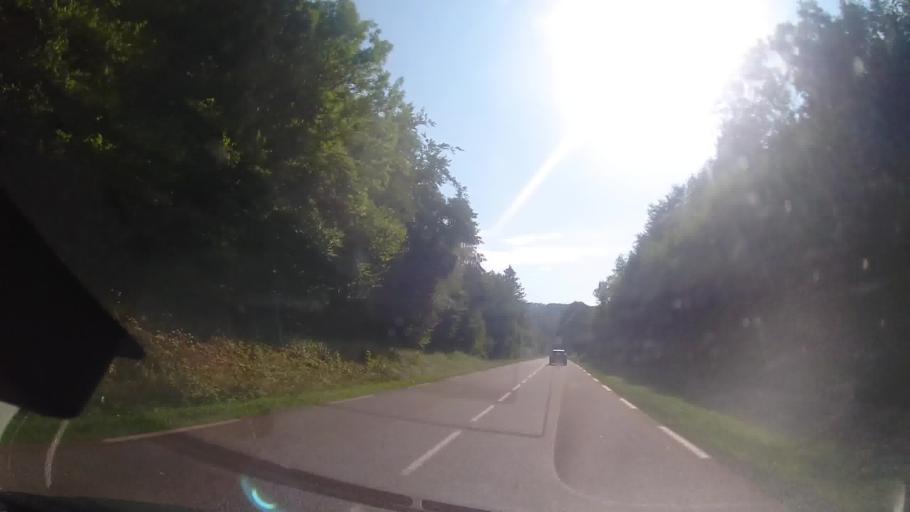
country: FR
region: Franche-Comte
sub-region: Departement du Jura
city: Clairvaux-les-Lacs
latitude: 46.5886
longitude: 5.8337
